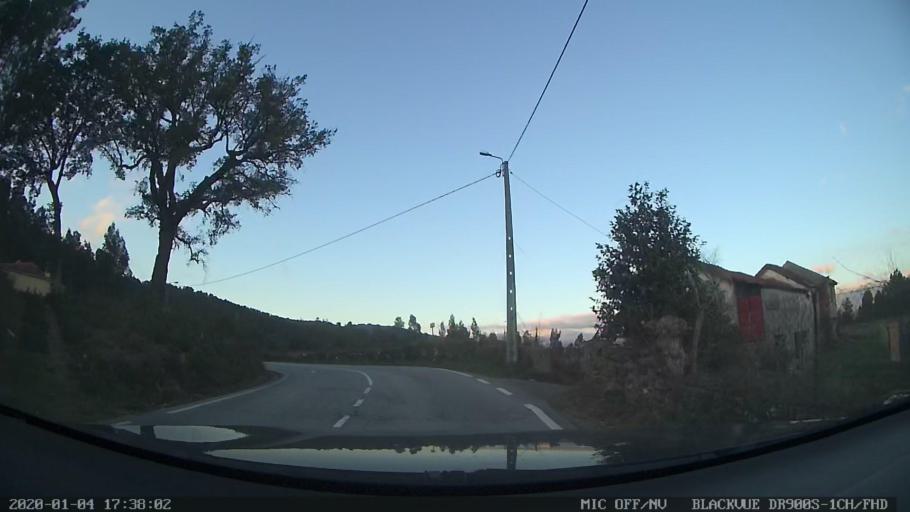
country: PT
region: Vila Real
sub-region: Mondim de Basto
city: Mondim de Basto
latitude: 41.4524
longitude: -7.9587
